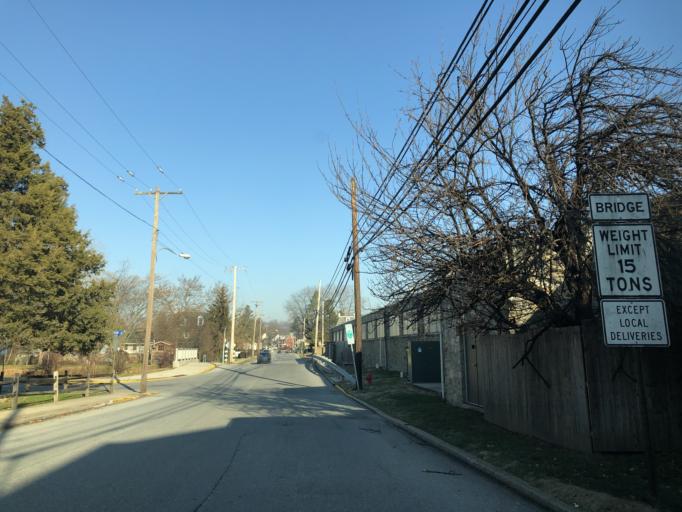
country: US
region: Pennsylvania
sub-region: Chester County
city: Downingtown
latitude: 40.0051
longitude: -75.6944
